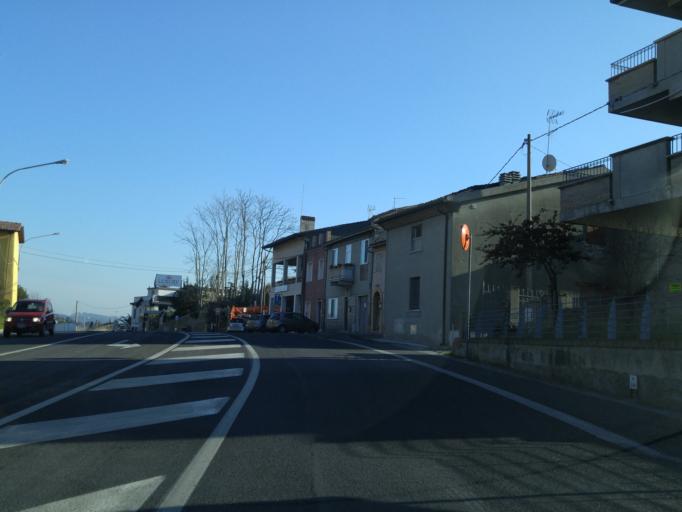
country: IT
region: The Marches
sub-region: Provincia di Pesaro e Urbino
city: Gradara
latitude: 43.9432
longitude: 12.8221
